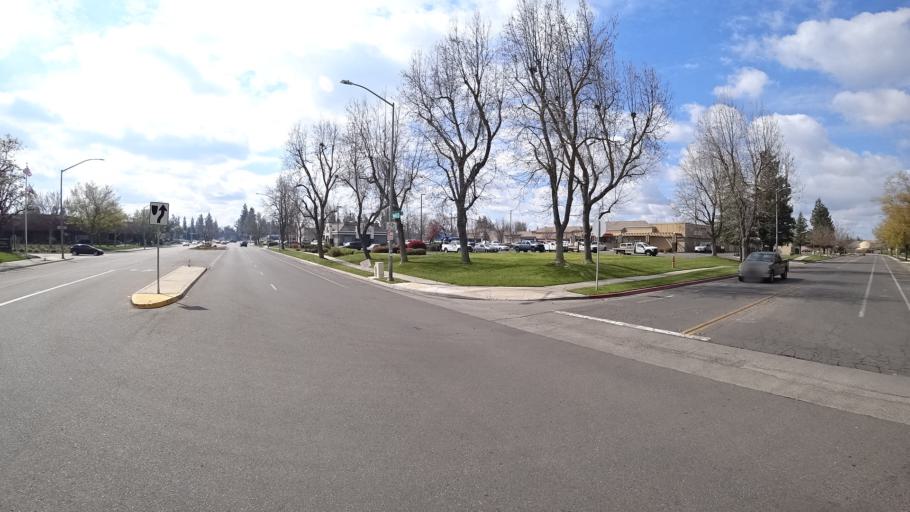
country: US
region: California
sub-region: Fresno County
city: Fresno
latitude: 36.8395
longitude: -119.8476
